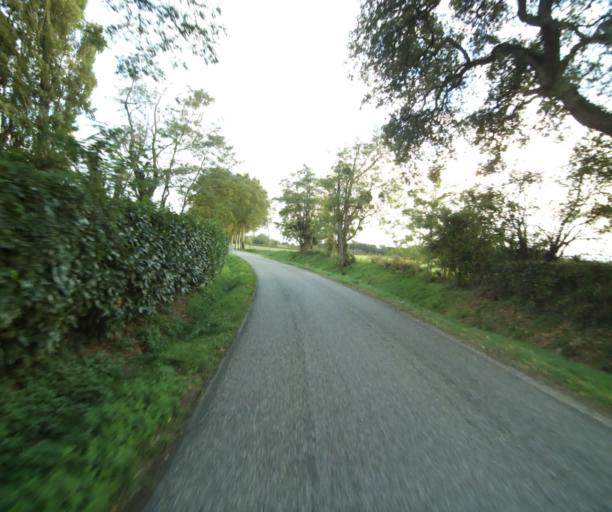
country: FR
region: Aquitaine
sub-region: Departement des Landes
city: Gabarret
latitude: 43.9614
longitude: 0.0877
